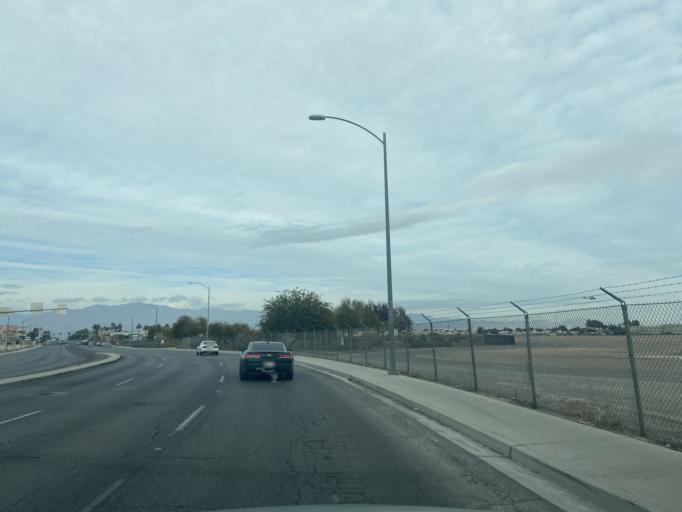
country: US
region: Nevada
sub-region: Clark County
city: Las Vegas
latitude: 36.2139
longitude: -115.2076
